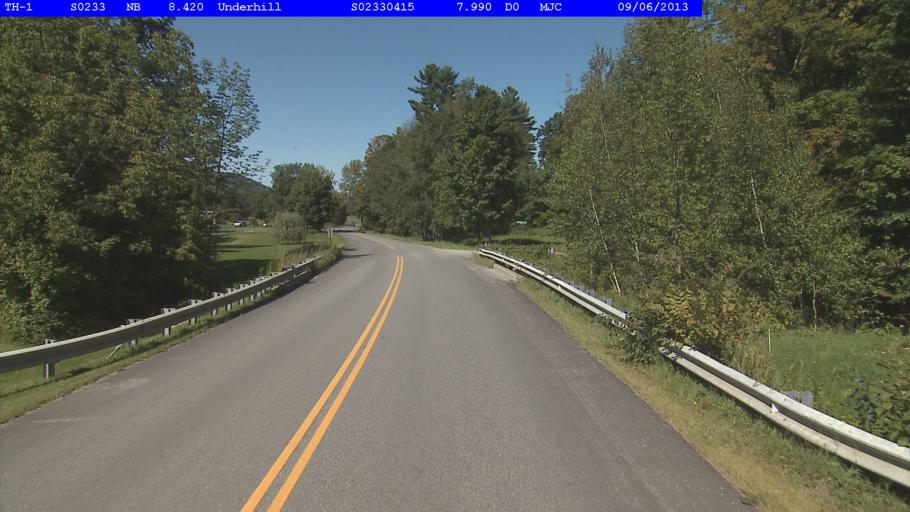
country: US
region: Vermont
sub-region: Chittenden County
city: Jericho
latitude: 44.5798
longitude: -72.8627
